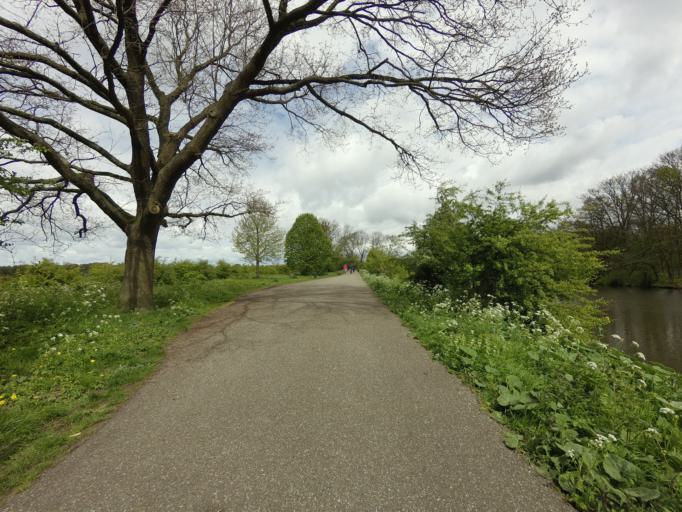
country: NL
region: North Holland
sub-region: Gemeente Naarden
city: Naarden
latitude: 52.2993
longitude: 5.1612
